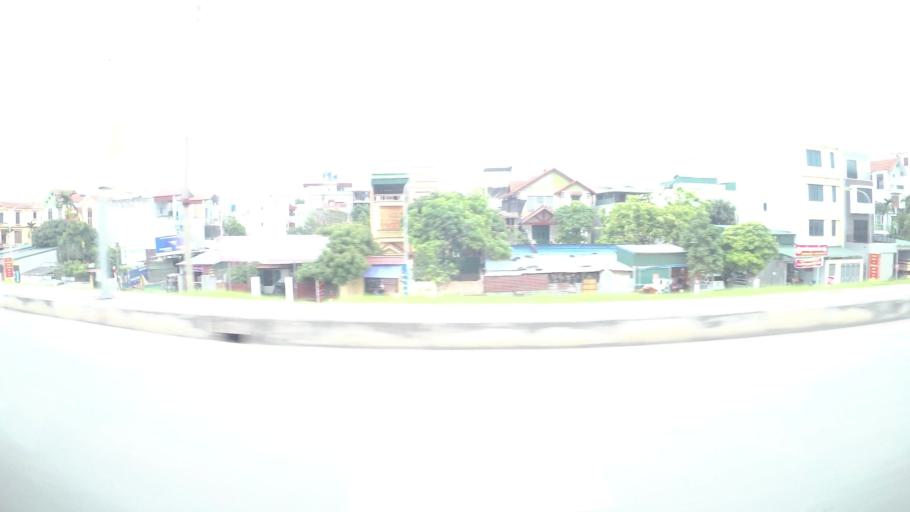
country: VN
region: Ha Noi
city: Hoan Kiem
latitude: 21.0665
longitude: 105.8713
